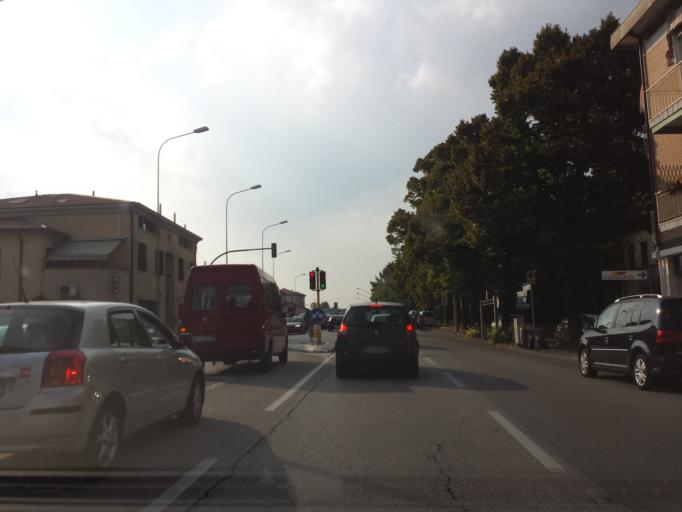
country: IT
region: Veneto
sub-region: Provincia di Padova
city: Caselle
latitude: 45.4169
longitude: 11.8288
